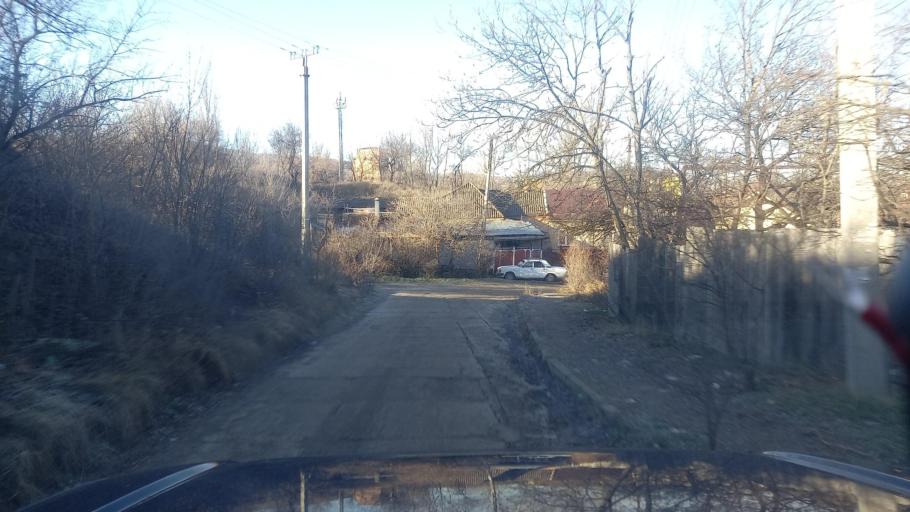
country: RU
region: Stavropol'skiy
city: Svobody
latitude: 44.0219
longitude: 43.0505
